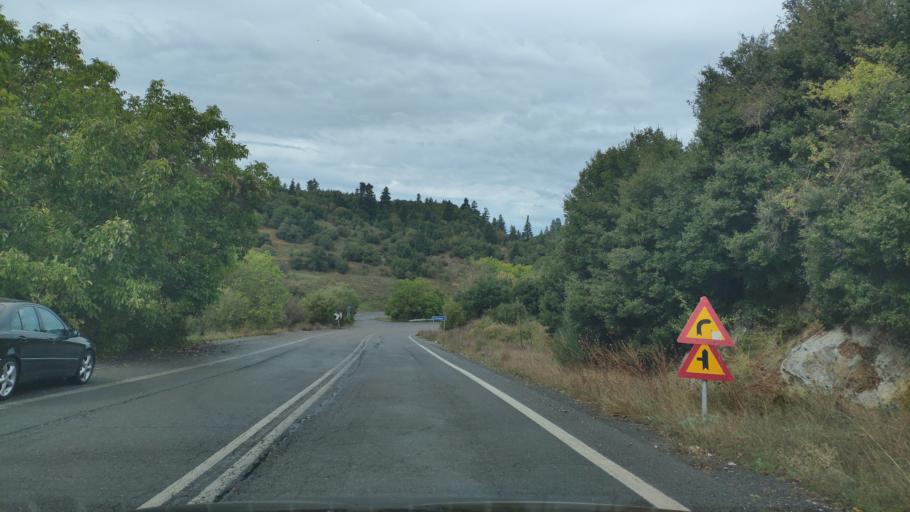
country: GR
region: Peloponnese
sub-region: Nomos Arkadias
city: Dimitsana
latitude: 37.6500
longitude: 22.1717
